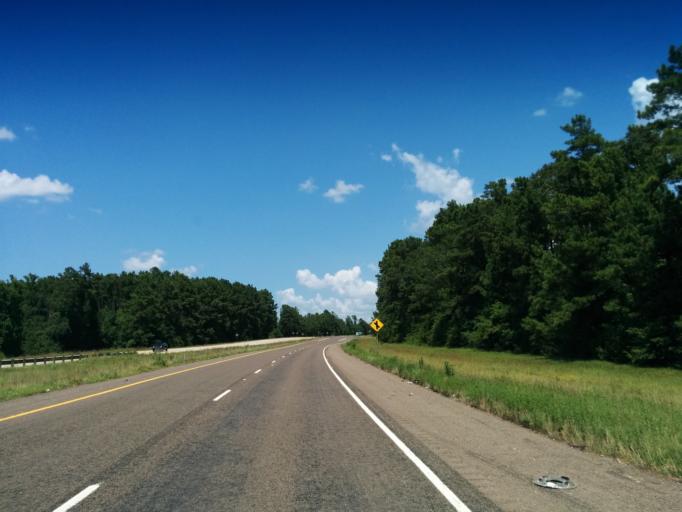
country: US
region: Texas
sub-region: Hardin County
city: Silsbee
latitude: 30.3192
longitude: -94.1795
